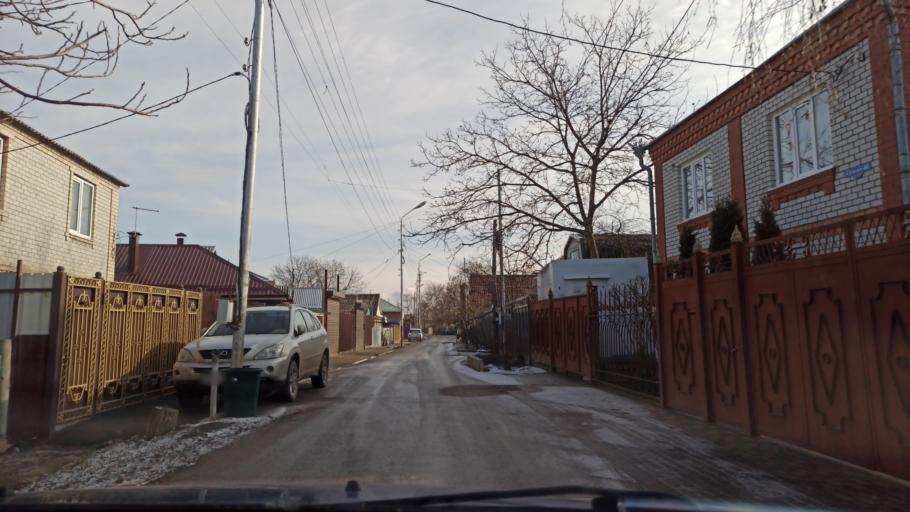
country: RU
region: Stavropol'skiy
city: Yessentukskaya
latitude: 44.0394
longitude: 42.8810
